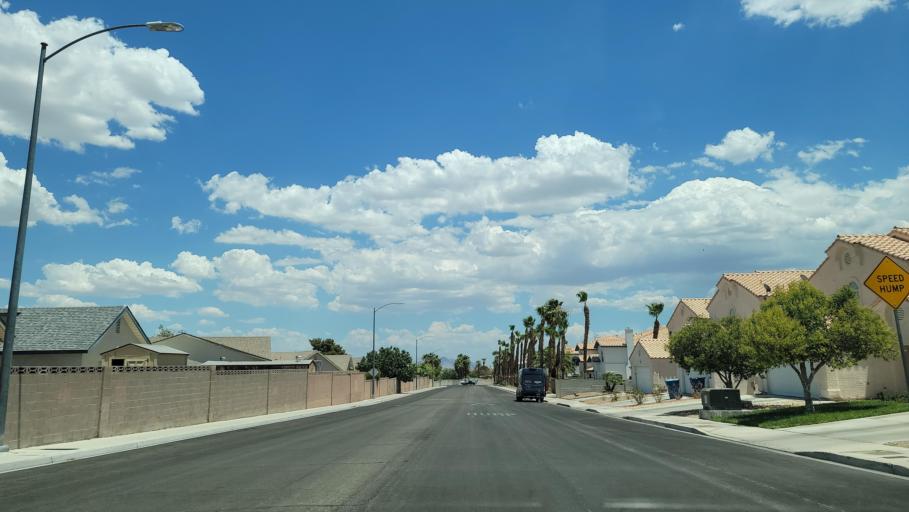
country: US
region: Nevada
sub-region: Clark County
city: Spring Valley
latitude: 36.1628
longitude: -115.2720
